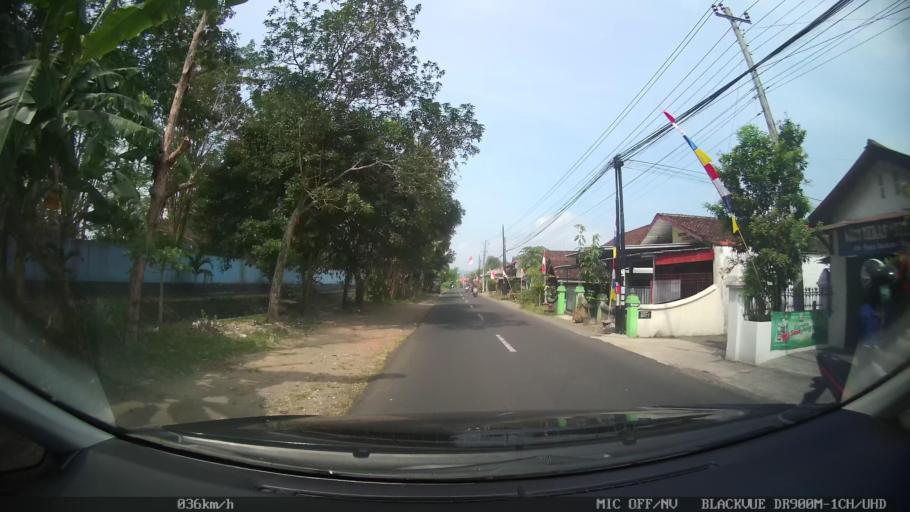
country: ID
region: Daerah Istimewa Yogyakarta
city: Depok
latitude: -7.8040
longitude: 110.4353
